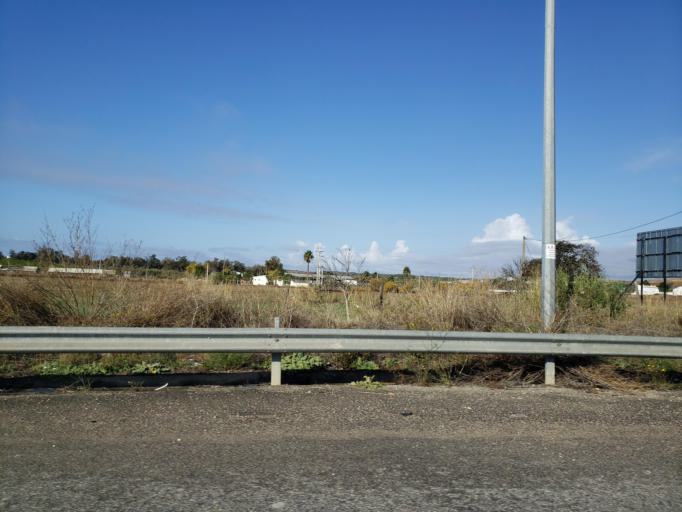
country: PT
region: Faro
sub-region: Portimao
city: Alvor
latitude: 37.1626
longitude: -8.5696
